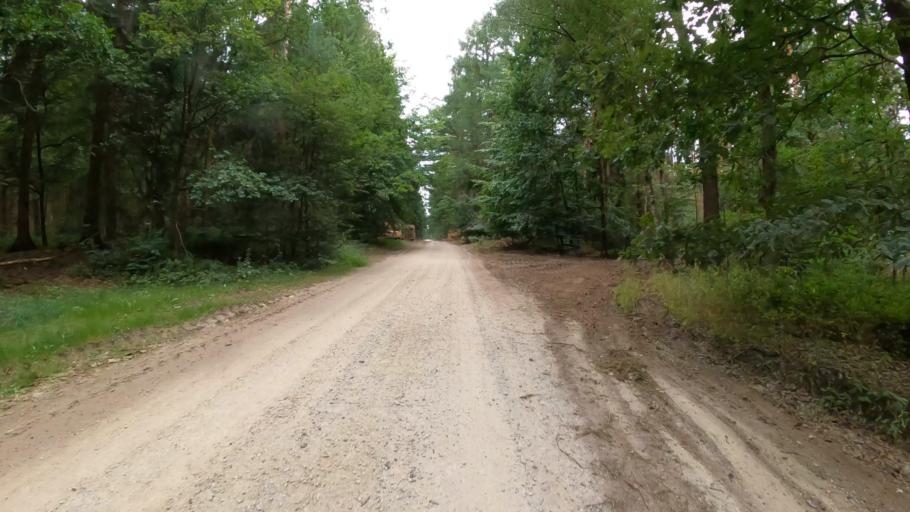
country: DE
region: Lower Saxony
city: Kakenstorf
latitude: 53.3149
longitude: 9.7386
